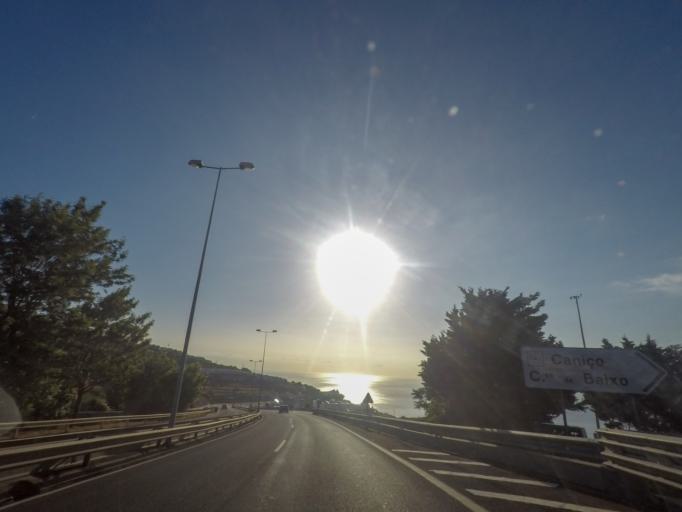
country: PT
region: Madeira
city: Canico
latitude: 32.6484
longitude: -16.8343
